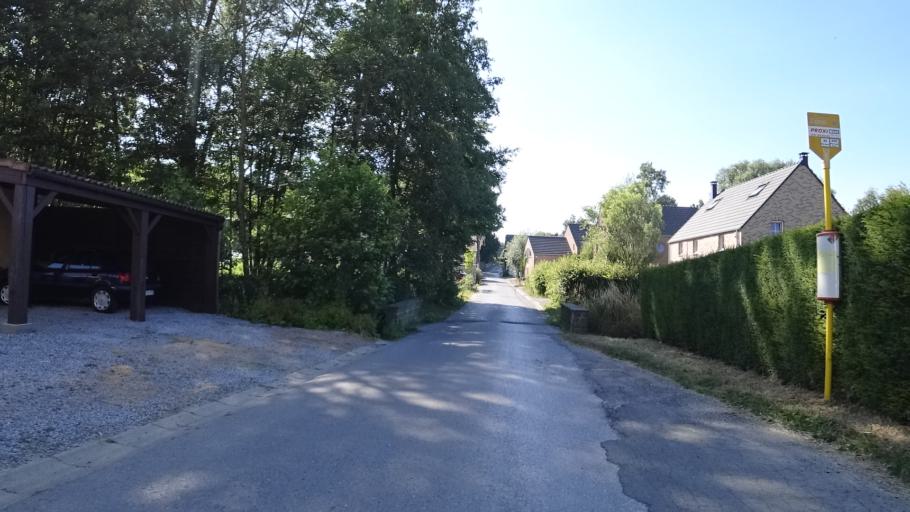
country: BE
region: Wallonia
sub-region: Province du Brabant Wallon
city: Incourt
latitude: 50.6699
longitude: 4.8043
